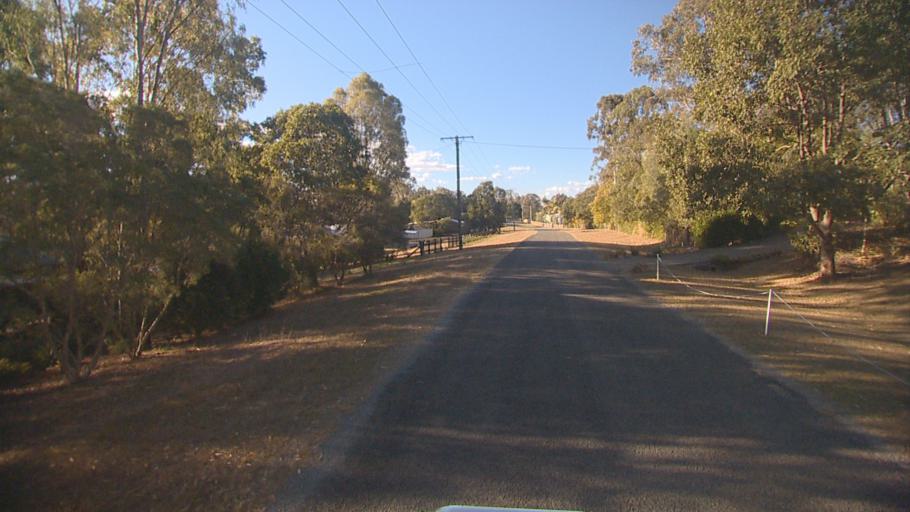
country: AU
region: Queensland
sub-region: Logan
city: Cedar Vale
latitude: -27.8553
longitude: 152.9812
